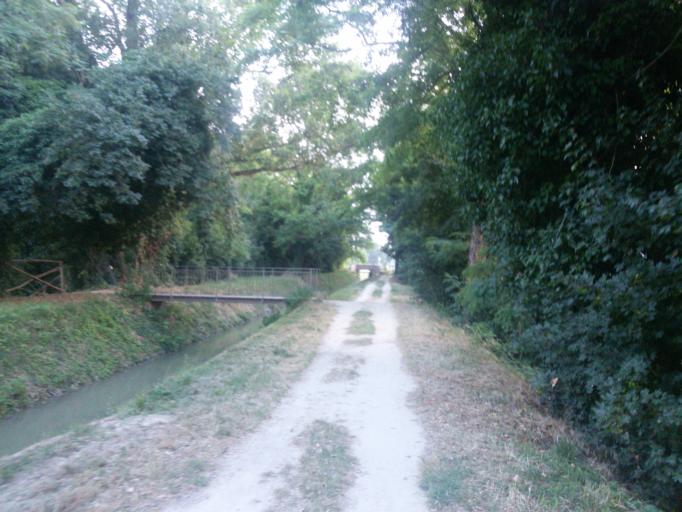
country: IT
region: Emilia-Romagna
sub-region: Provincia di Ravenna
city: Lugo
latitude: 44.4196
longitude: 11.8998
